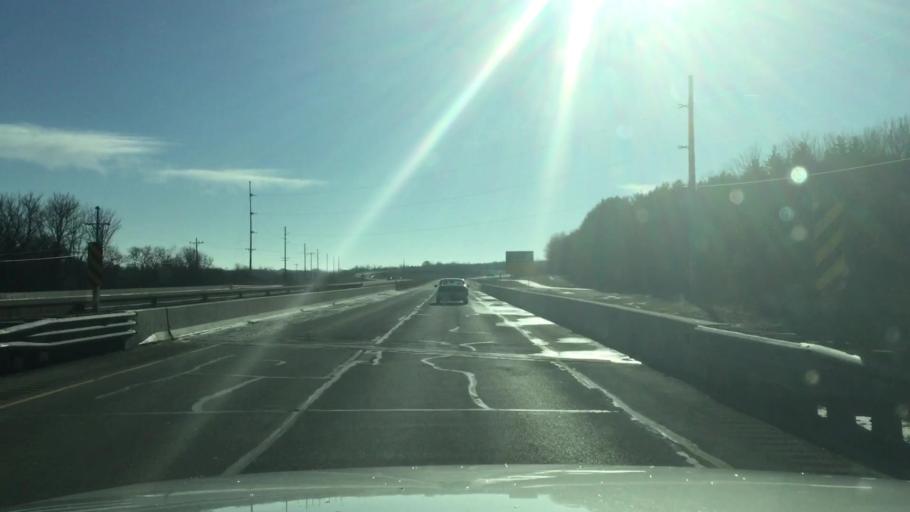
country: US
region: Wisconsin
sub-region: Racine County
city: Rochester
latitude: 42.7240
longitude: -88.2231
